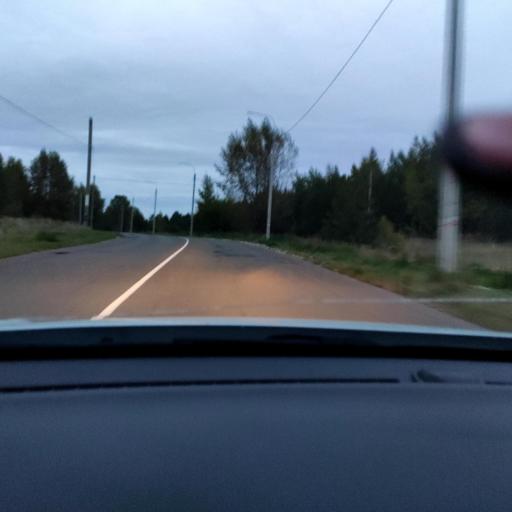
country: RU
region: Mariy-El
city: Volzhsk
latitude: 55.8729
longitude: 48.3759
